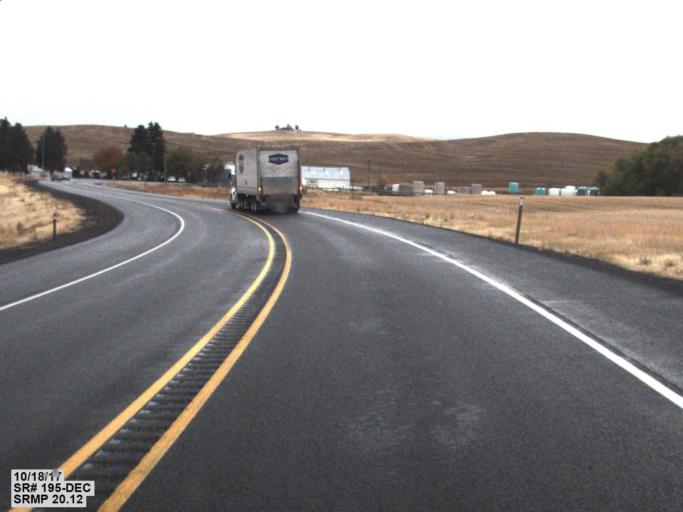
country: US
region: Washington
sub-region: Whitman County
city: Pullman
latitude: 46.7076
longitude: -117.2074
